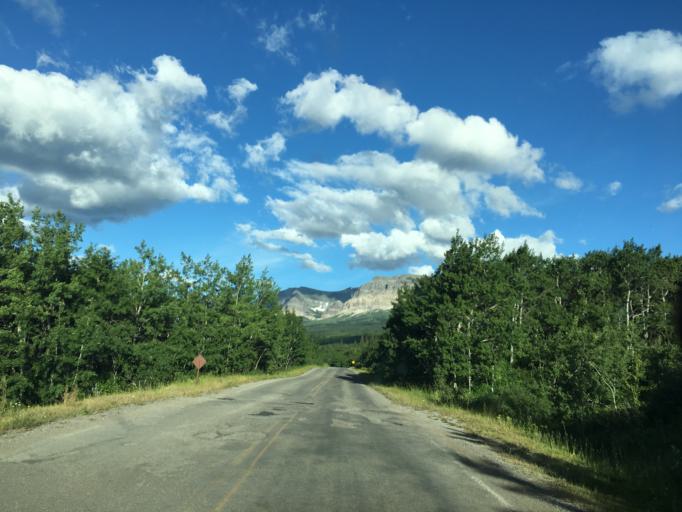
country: CA
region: Alberta
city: Cardston
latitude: 48.8301
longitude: -113.5281
